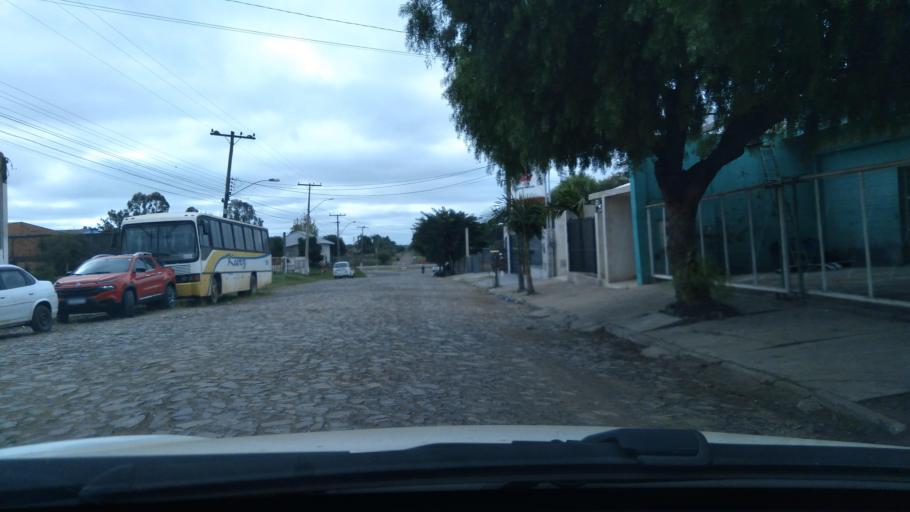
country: BR
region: Rio Grande do Sul
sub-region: Dom Pedrito
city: Dom Pedrito
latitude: -30.9649
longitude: -54.6723
